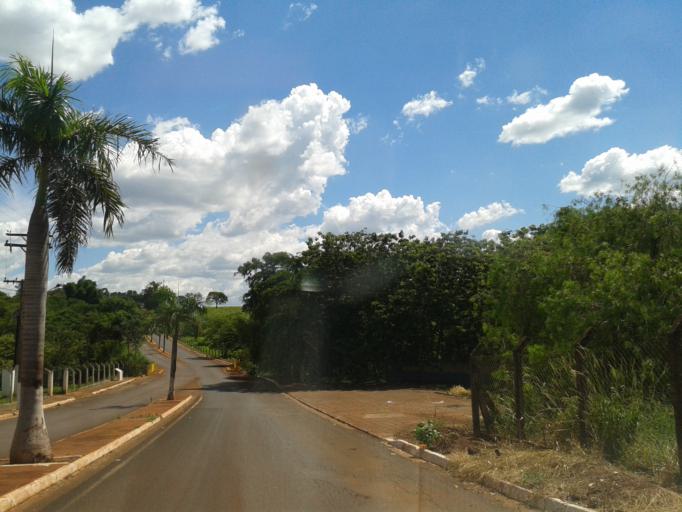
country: BR
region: Minas Gerais
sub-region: Centralina
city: Centralina
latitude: -18.7317
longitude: -49.2043
